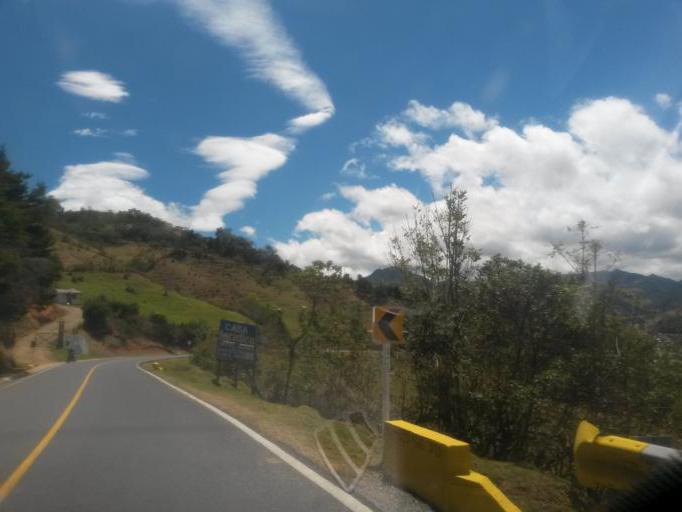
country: CO
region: Cauca
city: Silvia
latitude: 2.6056
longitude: -76.3901
